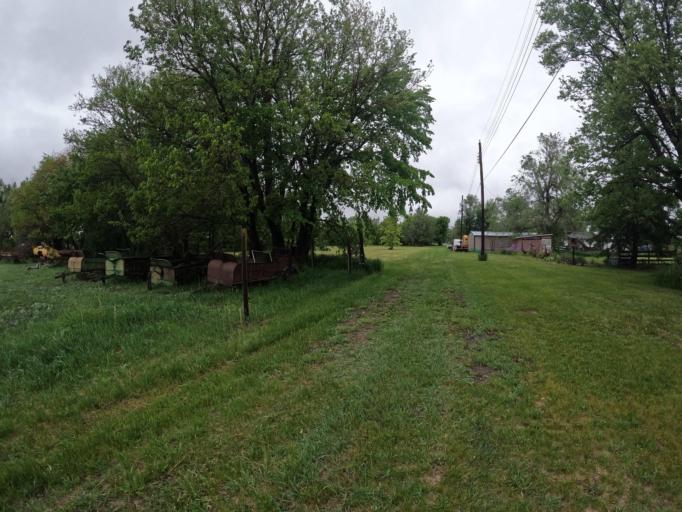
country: US
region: Nebraska
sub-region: Clay County
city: Harvard
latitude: 40.6240
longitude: -98.0992
